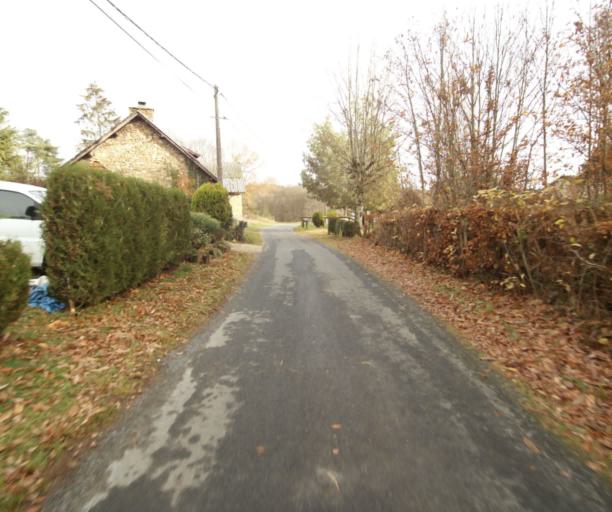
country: FR
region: Limousin
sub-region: Departement de la Correze
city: Sainte-Fortunade
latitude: 45.1912
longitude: 1.7870
